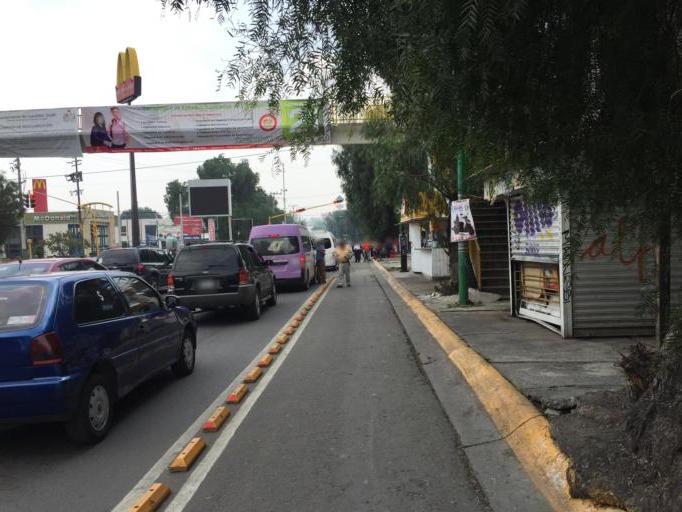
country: MX
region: Mexico
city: Cuautitlan Izcalli
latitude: 19.6491
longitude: -99.2049
